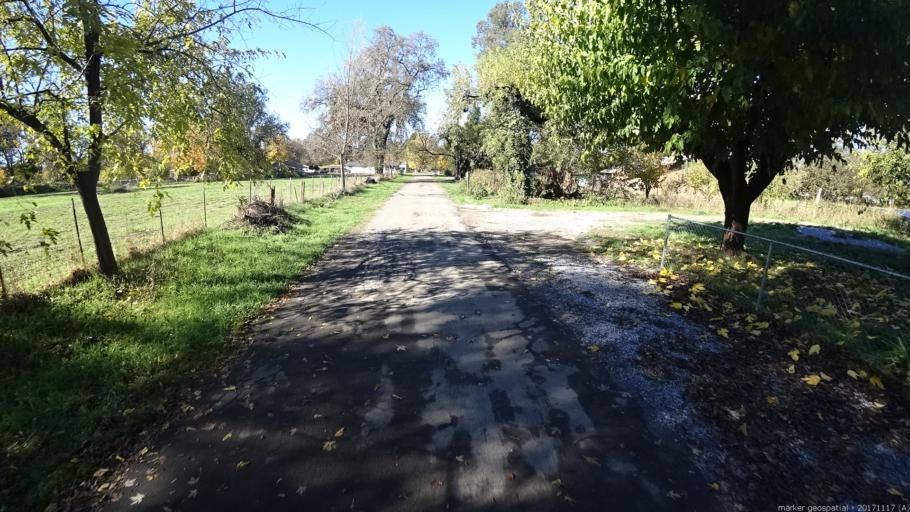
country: US
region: California
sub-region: Shasta County
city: Anderson
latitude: 40.4459
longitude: -122.2347
